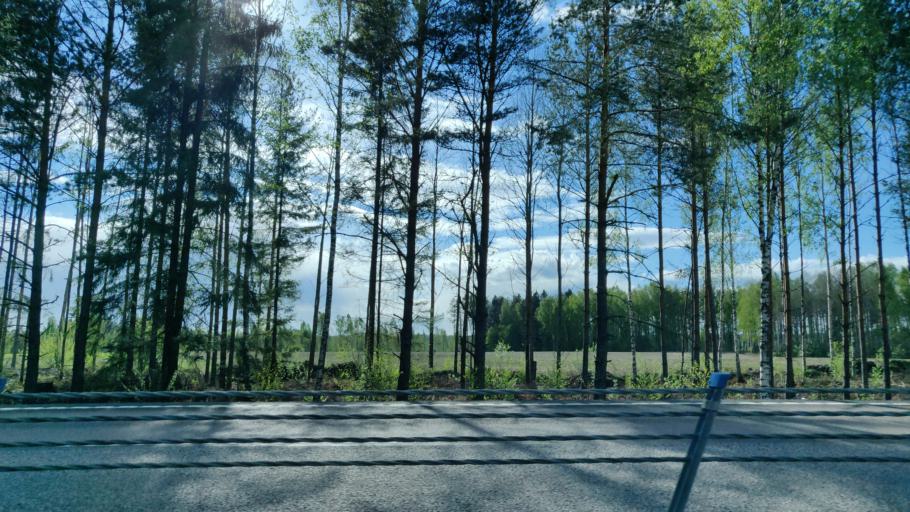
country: SE
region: Vaermland
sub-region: Forshaga Kommun
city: Forshaga
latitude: 59.4739
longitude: 13.4109
